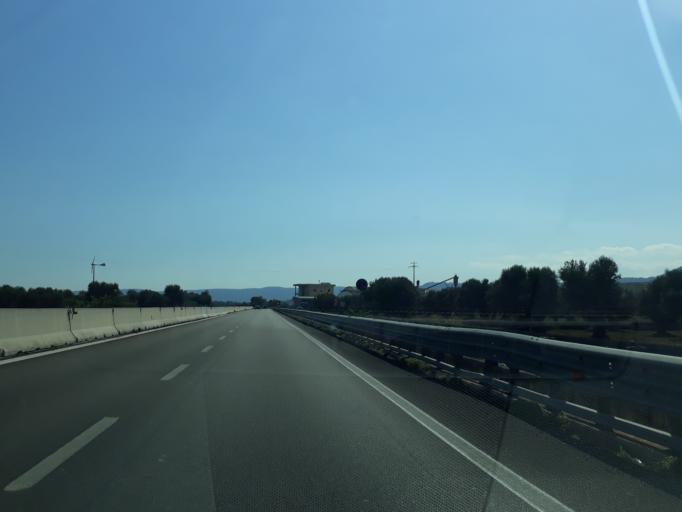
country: IT
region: Apulia
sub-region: Provincia di Brindisi
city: Fasano
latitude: 40.8626
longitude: 17.3474
